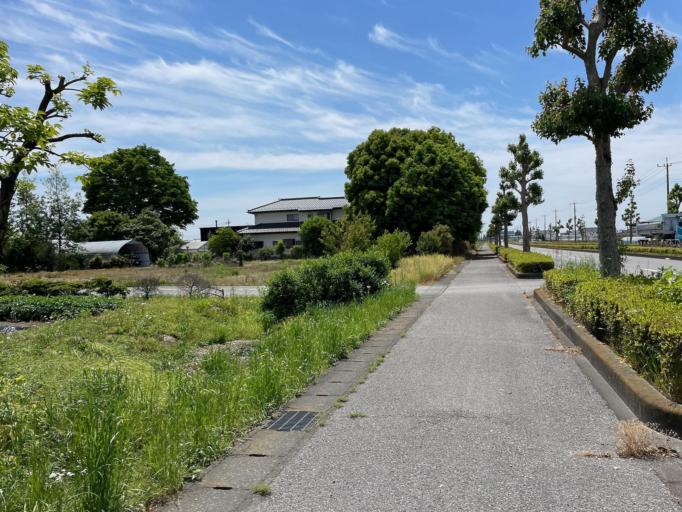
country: JP
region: Tochigi
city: Mibu
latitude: 36.4597
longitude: 139.7419
